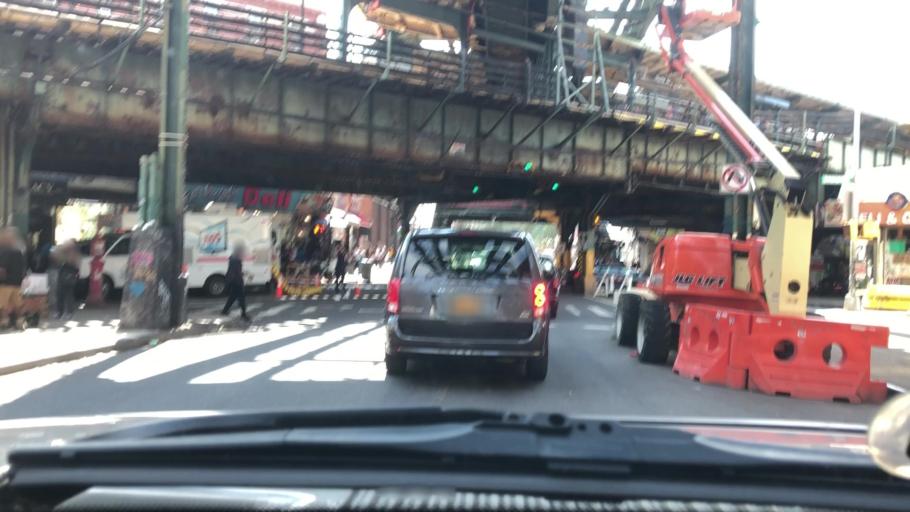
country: US
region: New York
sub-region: Kings County
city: Brooklyn
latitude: 40.6971
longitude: -73.9347
